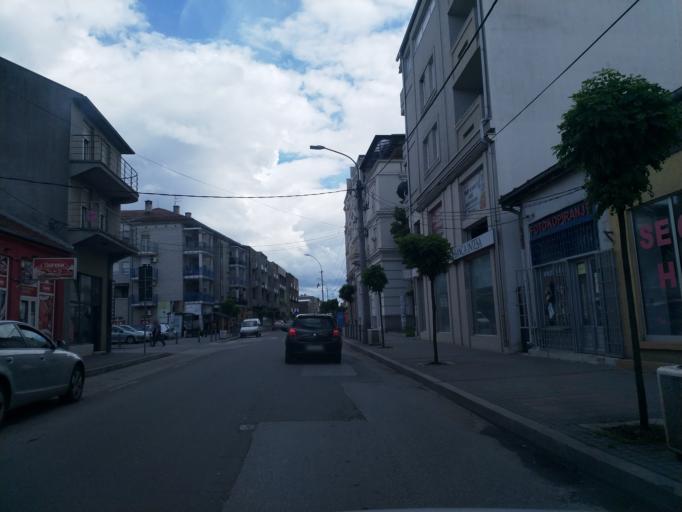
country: RS
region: Central Serbia
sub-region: Pomoravski Okrug
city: Cuprija
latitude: 43.9355
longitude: 21.3703
